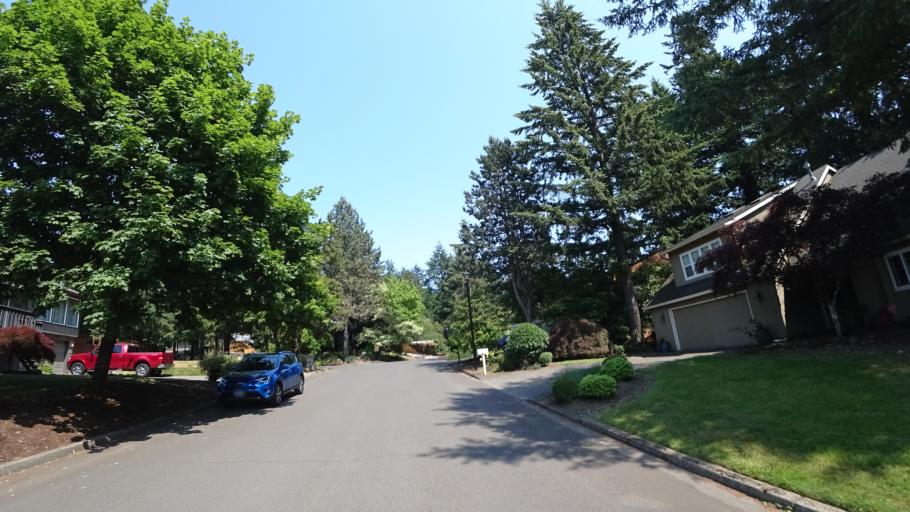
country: US
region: Oregon
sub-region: Multnomah County
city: Lents
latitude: 45.4471
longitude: -122.5637
